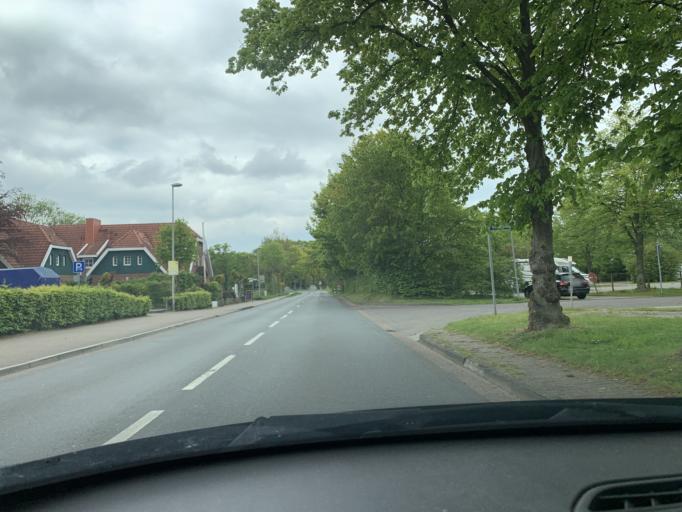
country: DE
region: Lower Saxony
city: Bad Zwischenahn
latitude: 53.2146
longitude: 8.0201
